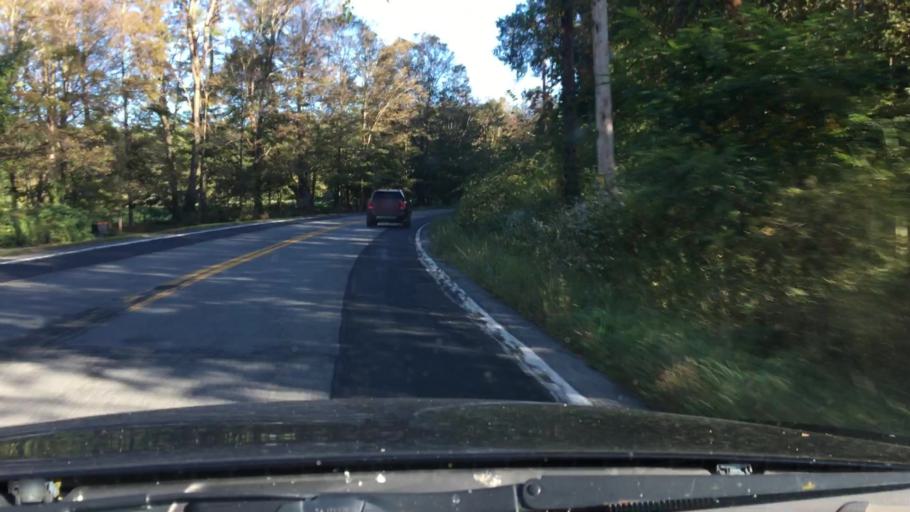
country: US
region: Connecticut
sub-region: Fairfield County
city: Sherman
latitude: 41.6529
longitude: -73.5316
